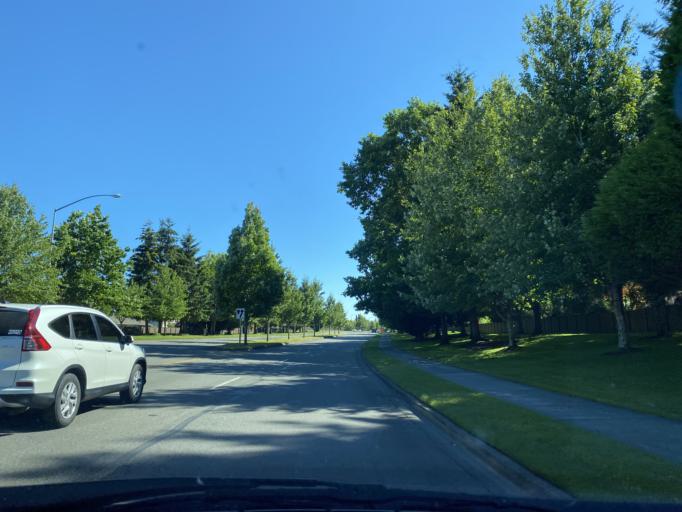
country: US
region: Washington
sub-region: Pierce County
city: McMillin
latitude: 47.1051
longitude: -122.2504
